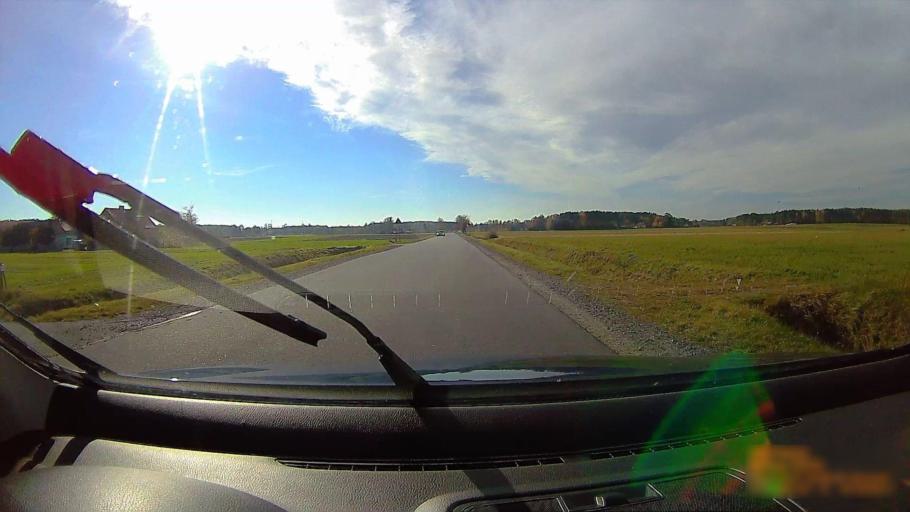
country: PL
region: Greater Poland Voivodeship
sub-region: Powiat ostrzeszowski
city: Doruchow
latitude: 51.3847
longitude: 18.0469
